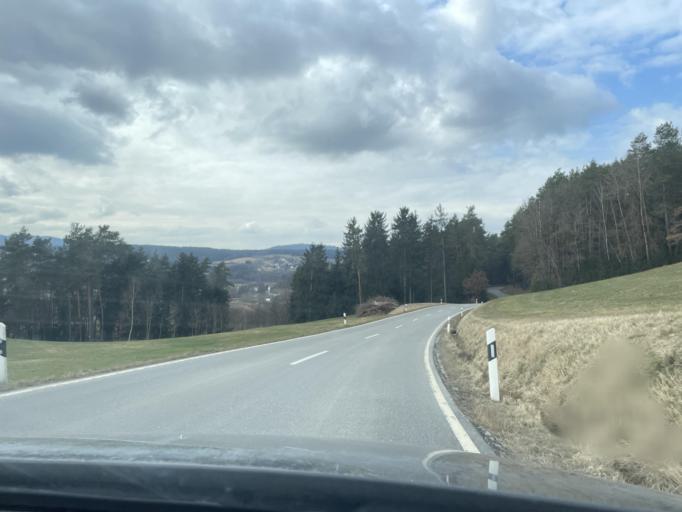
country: DE
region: Bavaria
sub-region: Lower Bavaria
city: Viechtach
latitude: 49.0908
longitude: 12.8993
